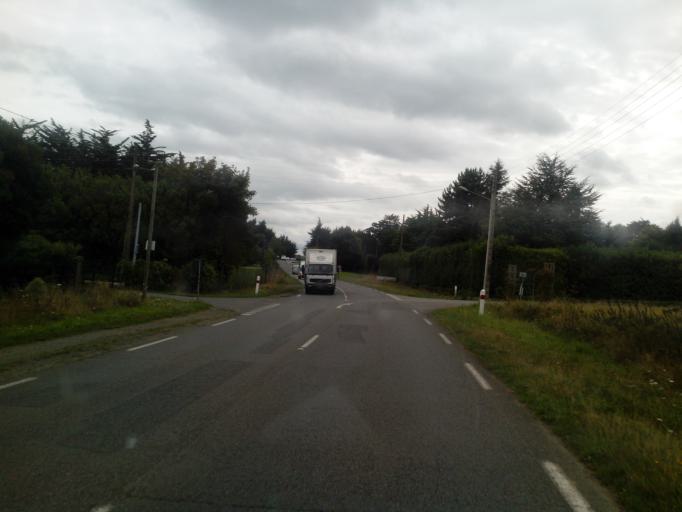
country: FR
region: Brittany
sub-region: Departement des Cotes-d'Armor
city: Etables-sur-Mer
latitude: 48.6275
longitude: -2.8257
